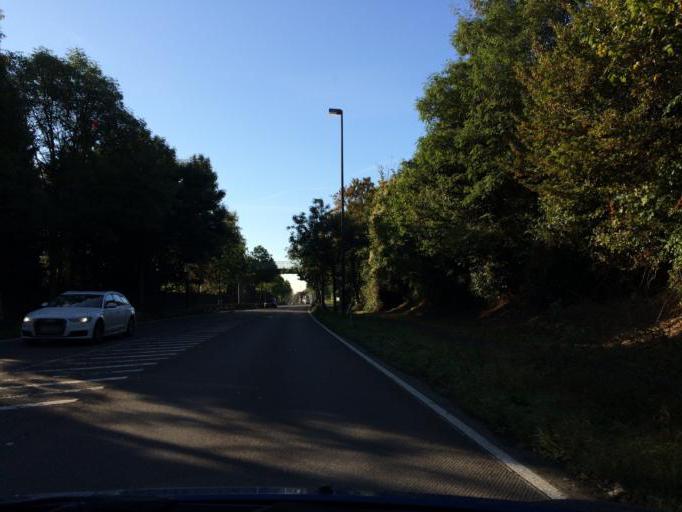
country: DE
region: North Rhine-Westphalia
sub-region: Regierungsbezirk Koln
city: Bonn
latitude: 50.7506
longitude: 7.1197
